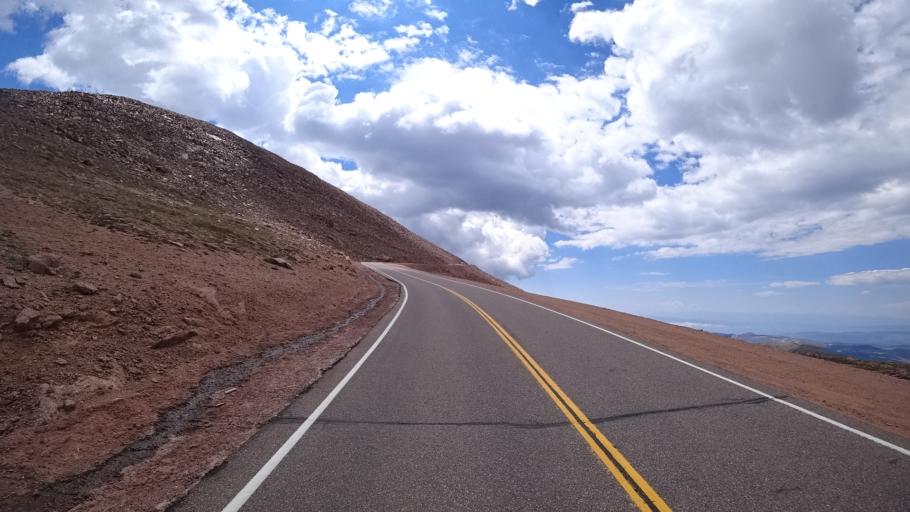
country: US
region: Colorado
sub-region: El Paso County
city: Cascade-Chipita Park
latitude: 38.8442
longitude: -105.0506
